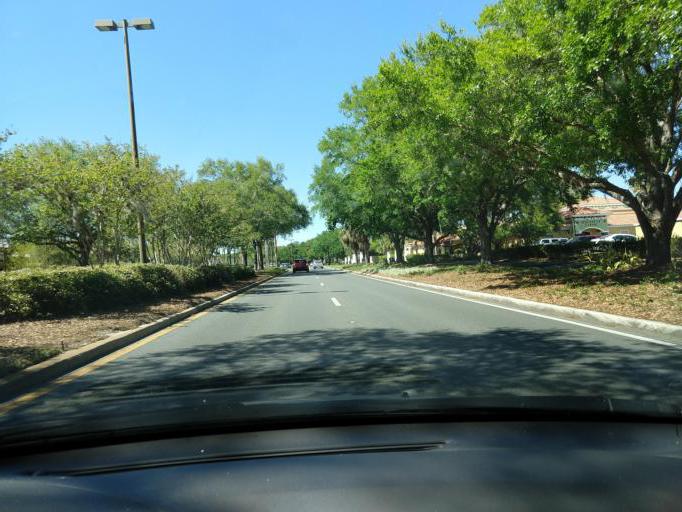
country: US
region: Florida
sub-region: Sumter County
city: The Villages
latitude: 28.9508
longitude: -81.9623
